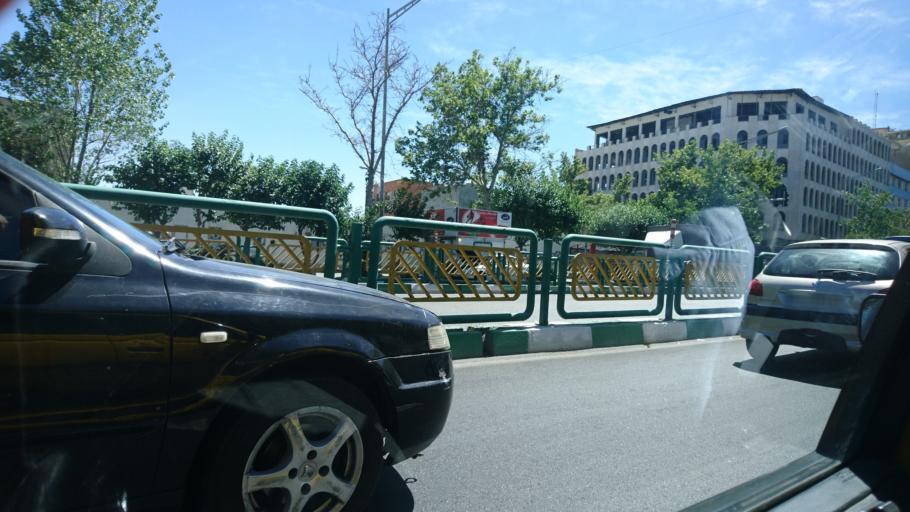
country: IR
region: Tehran
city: Tehran
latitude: 35.7012
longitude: 51.3993
